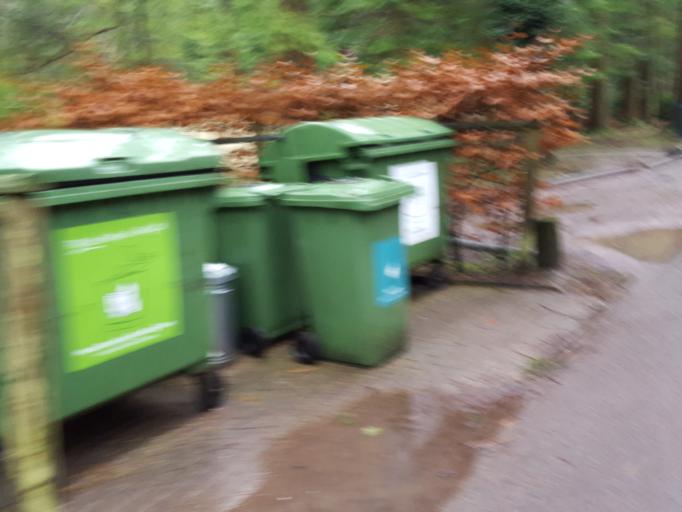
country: GB
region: England
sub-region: Wiltshire
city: Corsley
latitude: 51.1796
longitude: -2.2394
